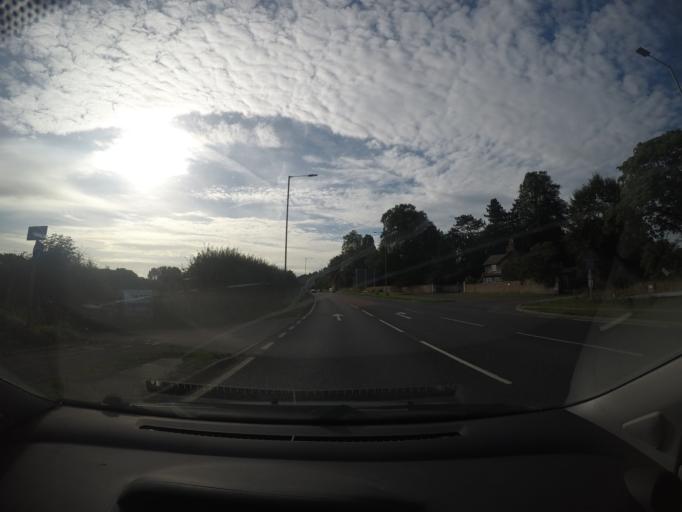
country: GB
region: England
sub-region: City of York
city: Fulford
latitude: 53.9225
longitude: -1.0648
